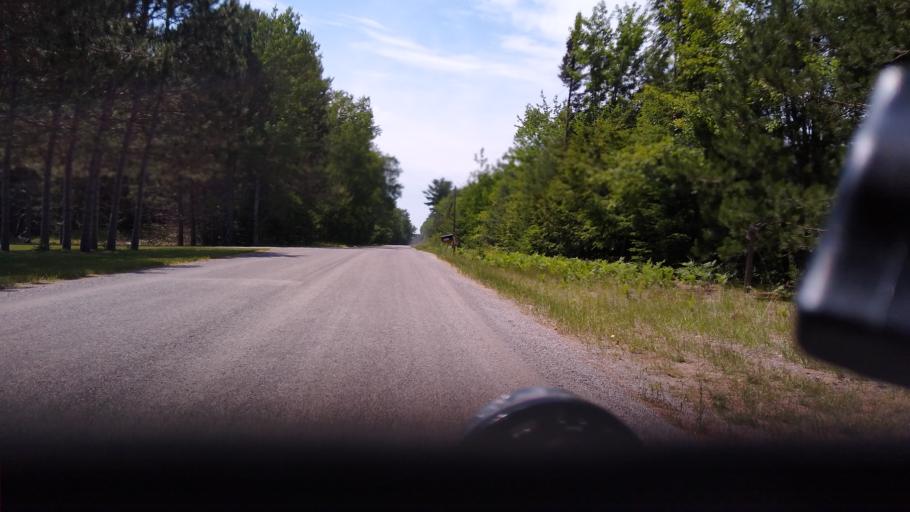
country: US
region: Michigan
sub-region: Delta County
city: Escanaba
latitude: 45.7102
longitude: -87.1498
